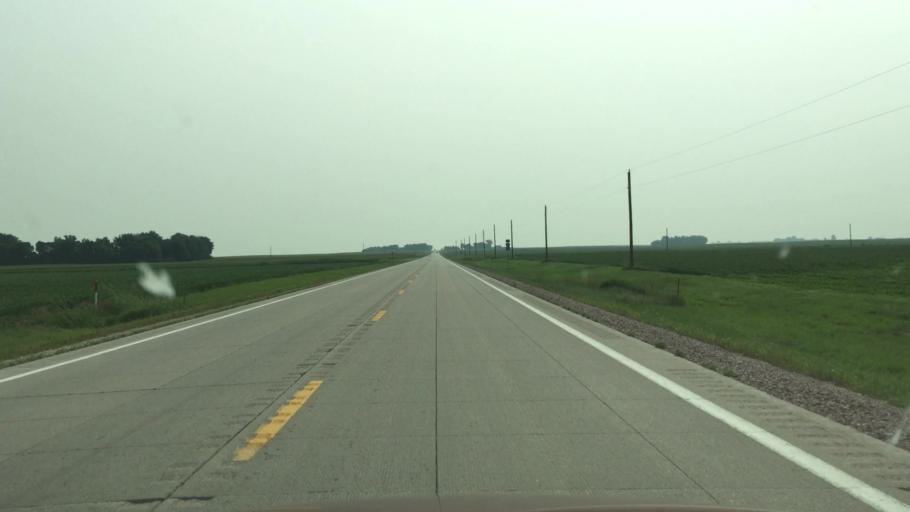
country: US
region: Iowa
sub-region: Osceola County
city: Sibley
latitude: 43.4327
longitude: -95.6868
